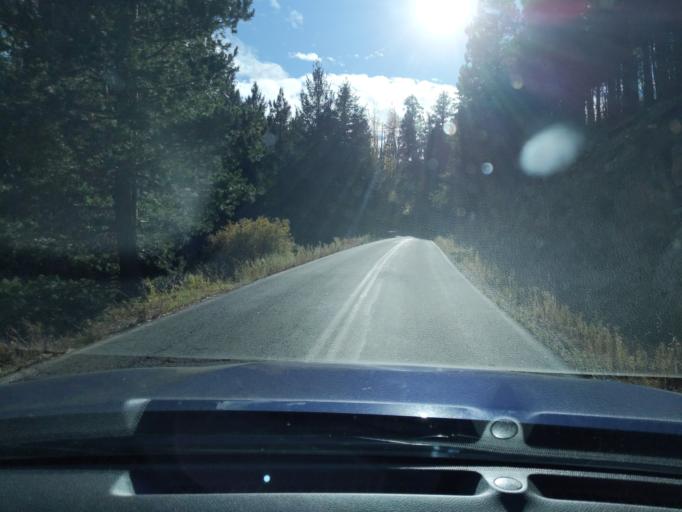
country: US
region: Arizona
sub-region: Pima County
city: Catalina
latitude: 32.4466
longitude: -110.7871
